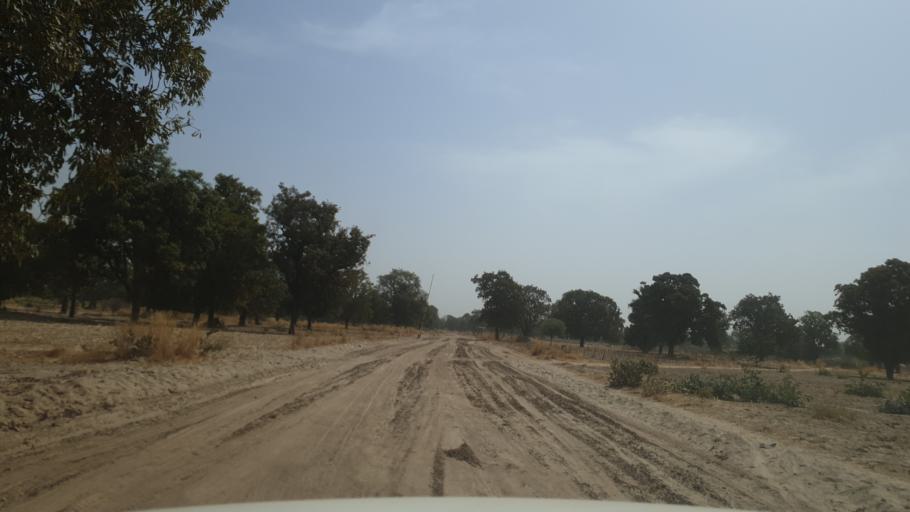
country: ML
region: Koulikoro
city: Kolokani
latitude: 13.4991
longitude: -8.2234
